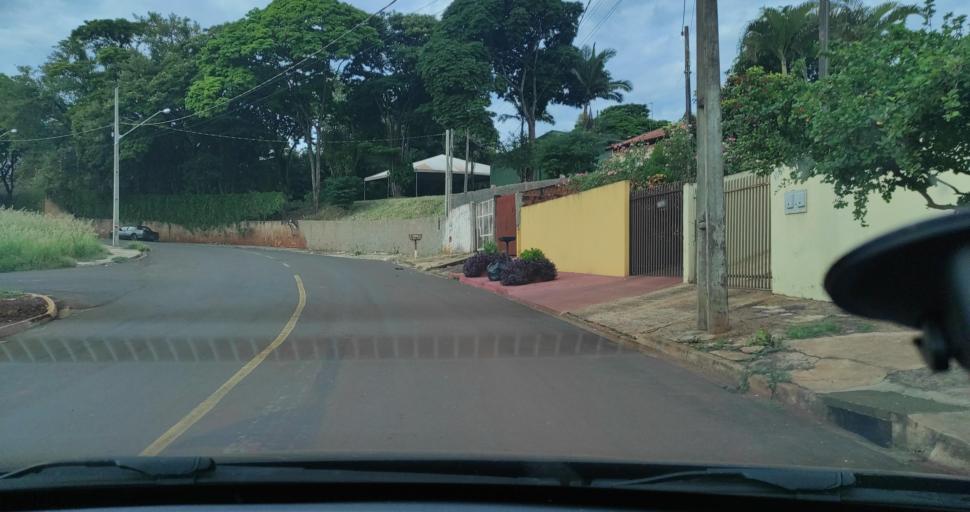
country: BR
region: Parana
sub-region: Ibipora
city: Ibipora
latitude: -23.2629
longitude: -51.0474
